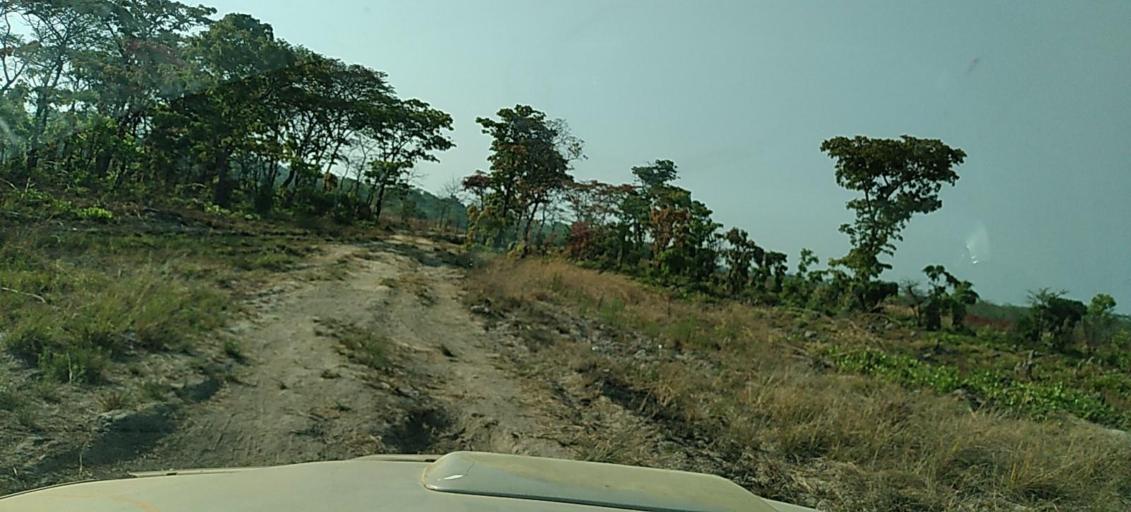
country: ZM
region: North-Western
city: Kasempa
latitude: -13.1888
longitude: 25.9688
